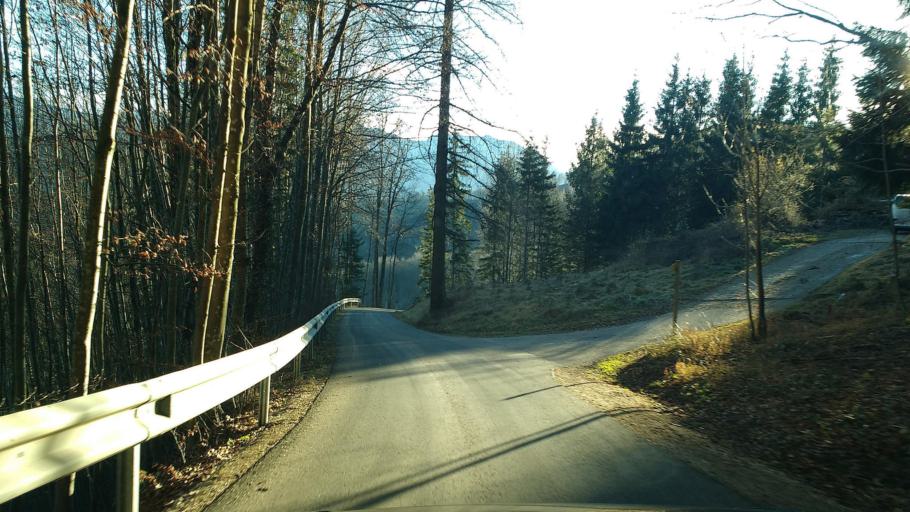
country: AT
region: Upper Austria
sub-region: Politischer Bezirk Kirchdorf an der Krems
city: Micheldorf in Oberoesterreich
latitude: 47.8952
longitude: 14.2172
